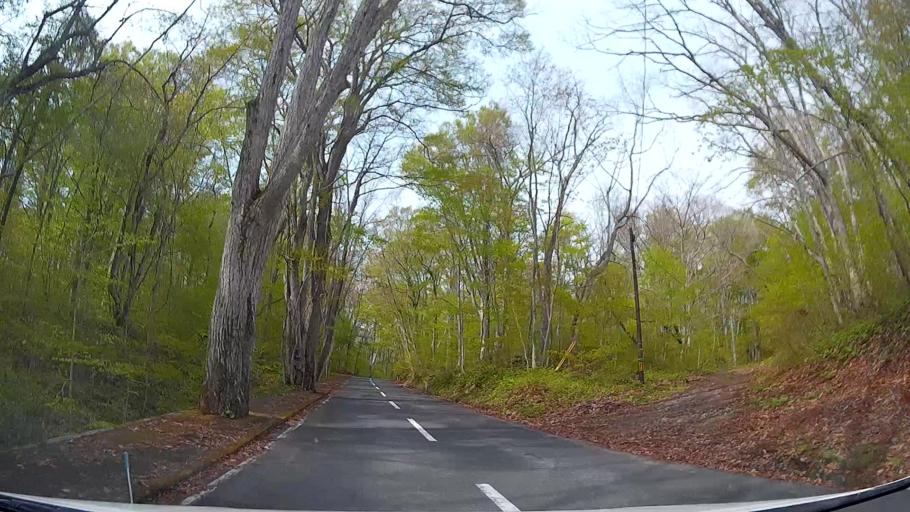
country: JP
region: Akita
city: Hanawa
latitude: 40.4325
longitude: 140.9154
